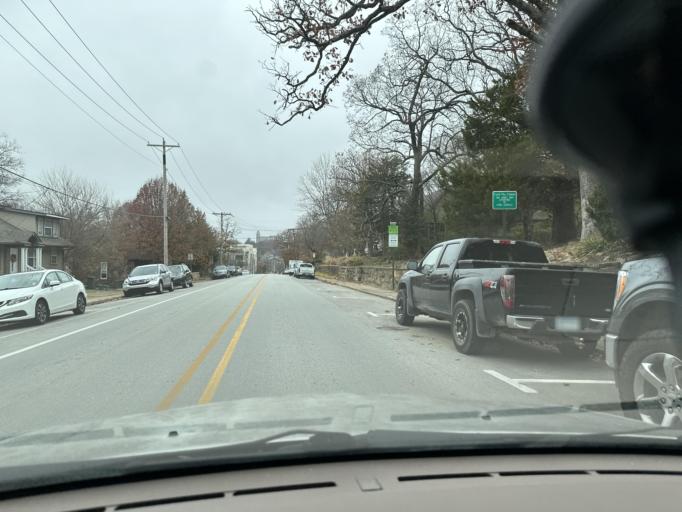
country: US
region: Arkansas
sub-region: Washington County
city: Fayetteville
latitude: 36.0686
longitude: -94.1610
